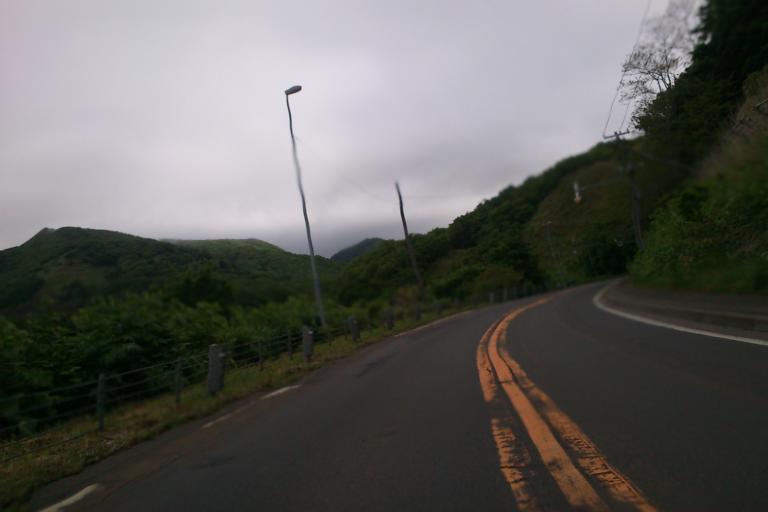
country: JP
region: Hokkaido
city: Ishikari
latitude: 43.4117
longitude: 141.4309
